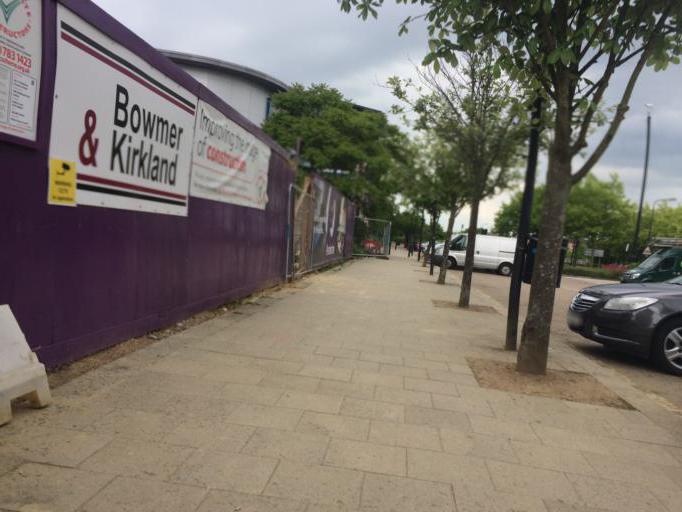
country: GB
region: England
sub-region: Milton Keynes
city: Milton Keynes
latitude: 52.0430
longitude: -0.7493
